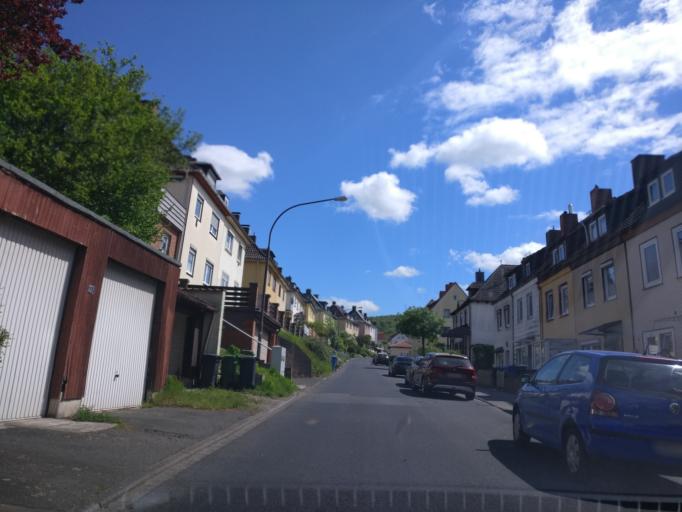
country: DE
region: Lower Saxony
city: Hannoversch Munden
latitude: 51.4061
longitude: 9.6598
